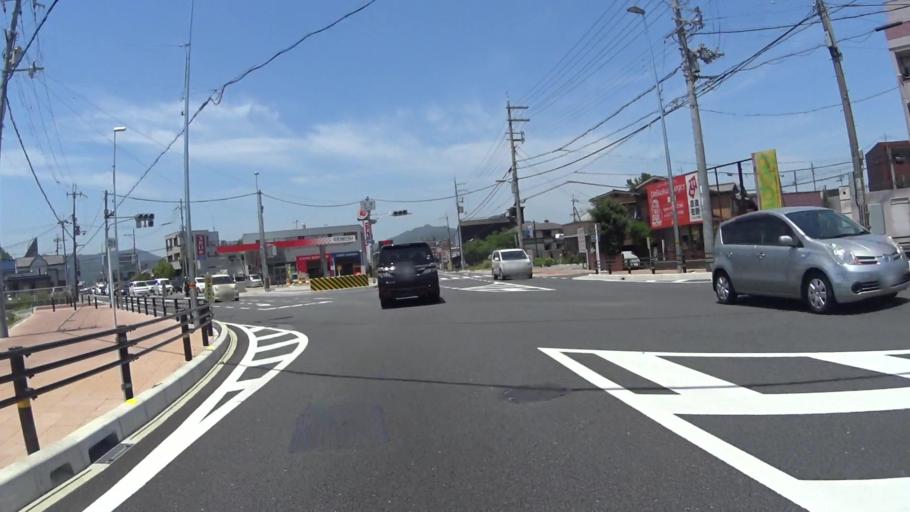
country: JP
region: Kyoto
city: Kameoka
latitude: 35.0137
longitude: 135.5714
